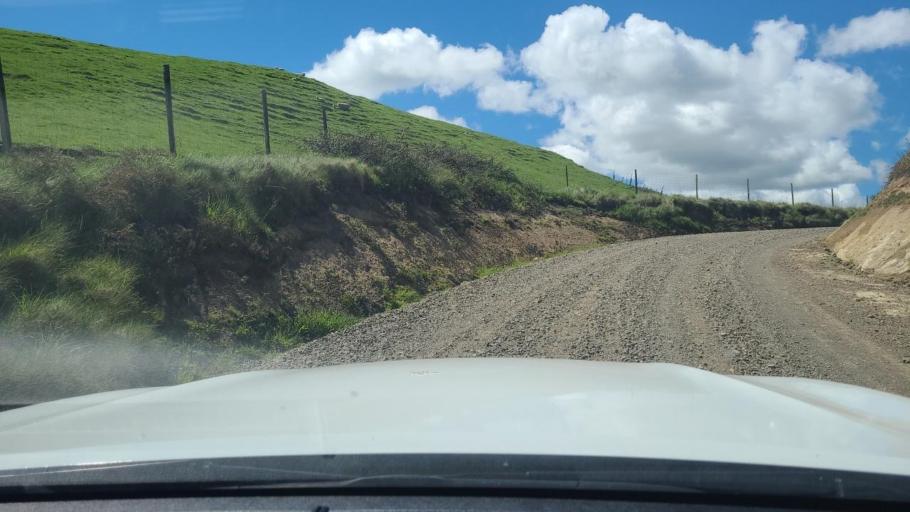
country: NZ
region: Hawke's Bay
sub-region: Napier City
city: Napier
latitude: -39.1532
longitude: 176.6588
